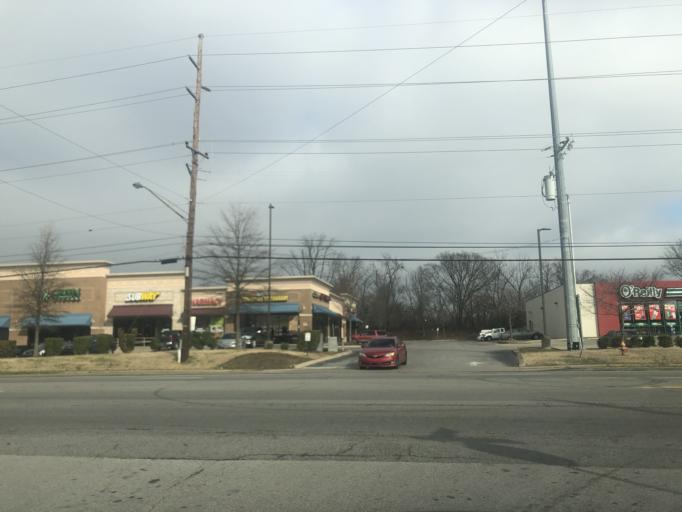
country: US
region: Tennessee
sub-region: Rutherford County
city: La Vergne
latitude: 36.0782
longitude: -86.6431
